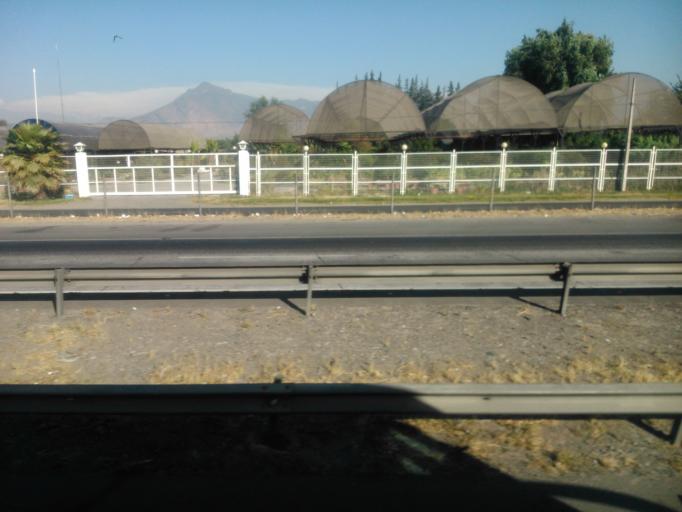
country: CL
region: Santiago Metropolitan
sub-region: Provincia de Maipo
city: Buin
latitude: -33.7236
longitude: -70.7290
